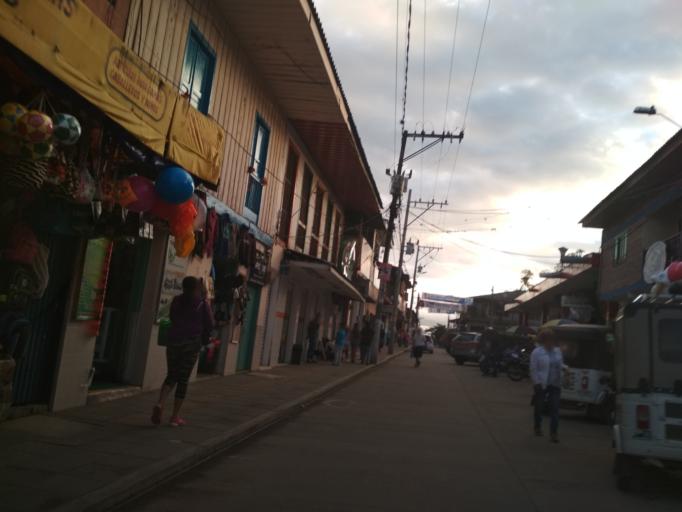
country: CO
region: Valle del Cauca
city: Calimita
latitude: 3.9316
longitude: -76.4846
